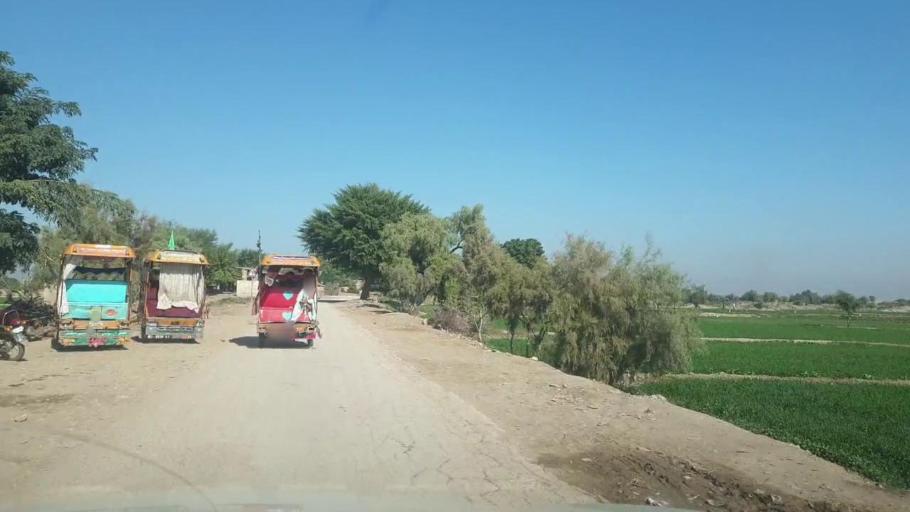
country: PK
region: Sindh
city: Bhan
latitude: 26.5538
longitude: 67.6334
